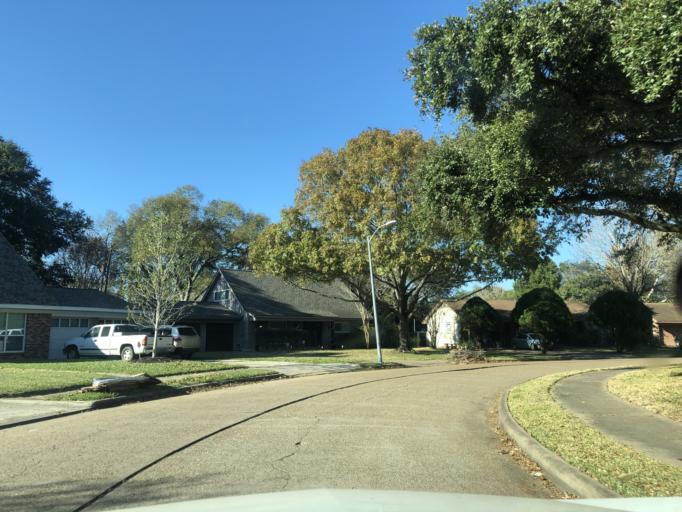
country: US
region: Texas
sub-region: Harris County
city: Bellaire
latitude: 29.6969
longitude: -95.5123
